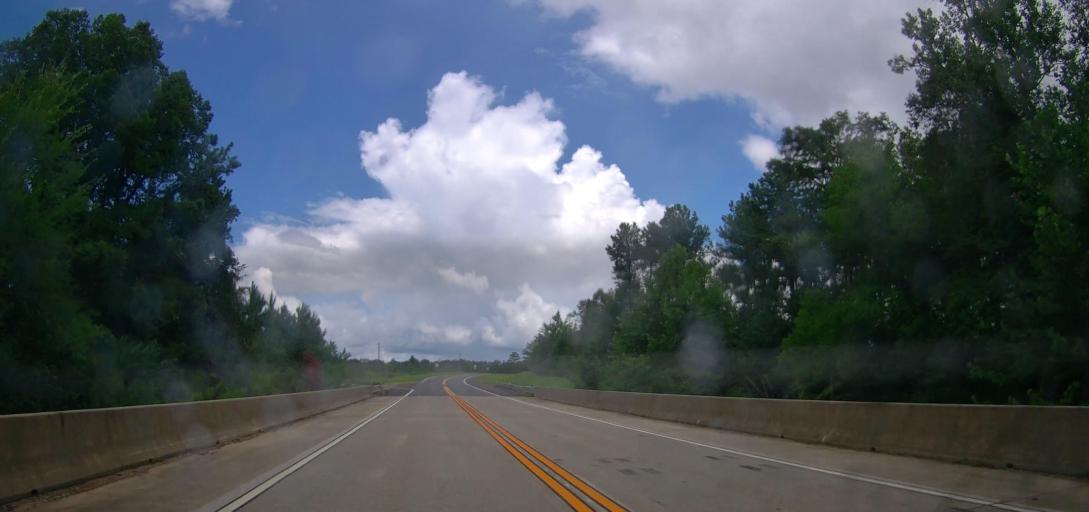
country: US
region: Georgia
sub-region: Pulaski County
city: Hawkinsville
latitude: 32.1603
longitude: -83.5472
